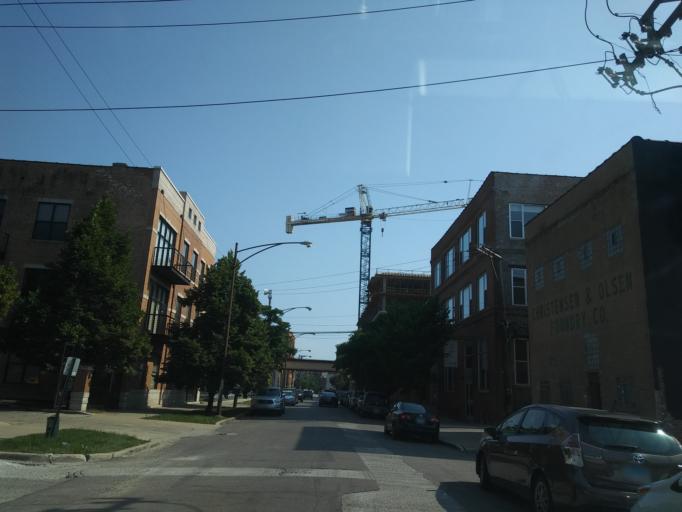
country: US
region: Illinois
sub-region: Cook County
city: Chicago
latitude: 41.8863
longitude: -87.6569
